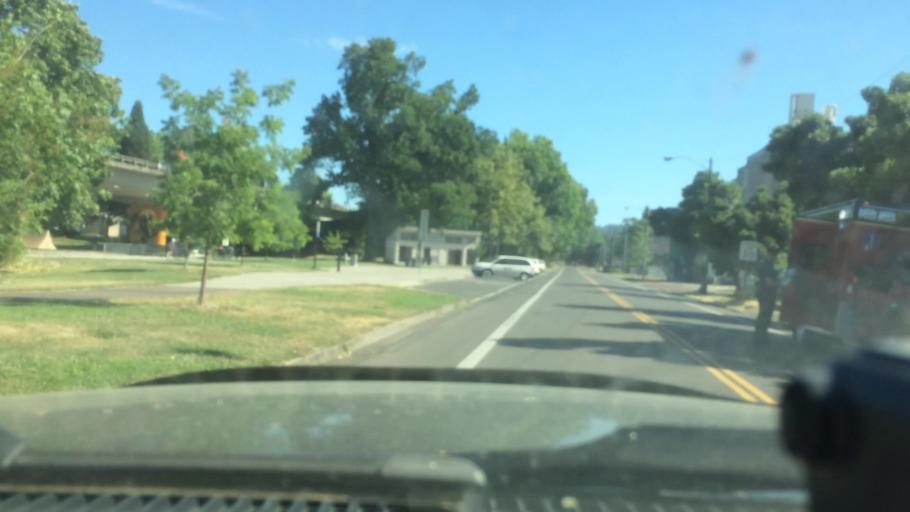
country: US
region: Oregon
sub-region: Lane County
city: Eugene
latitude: 44.0585
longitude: -123.1018
